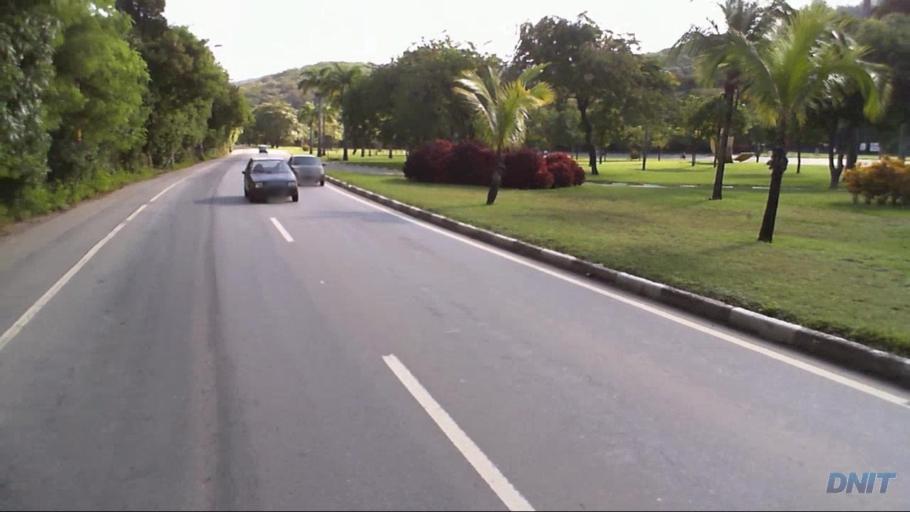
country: BR
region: Minas Gerais
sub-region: Ipatinga
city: Ipatinga
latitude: -19.4868
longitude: -42.5567
